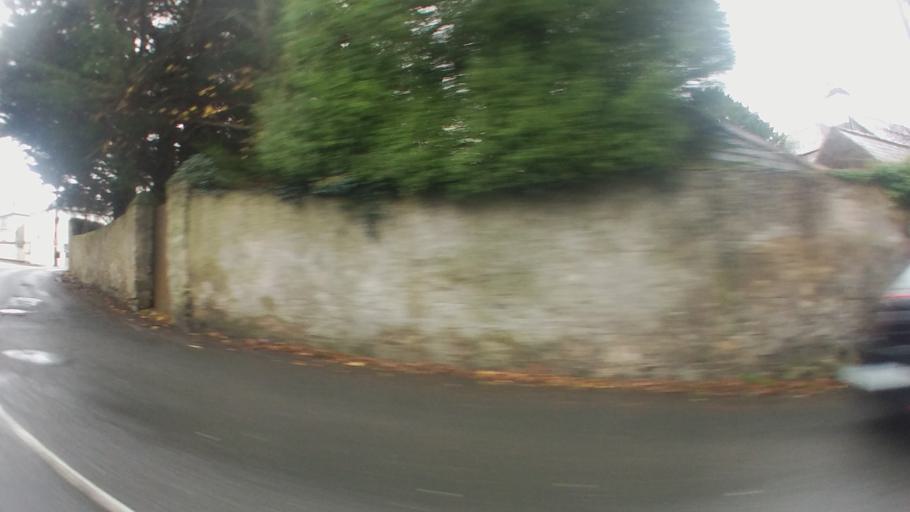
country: IE
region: Leinster
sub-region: Wicklow
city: Kilpedder
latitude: 53.1326
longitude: -6.0924
